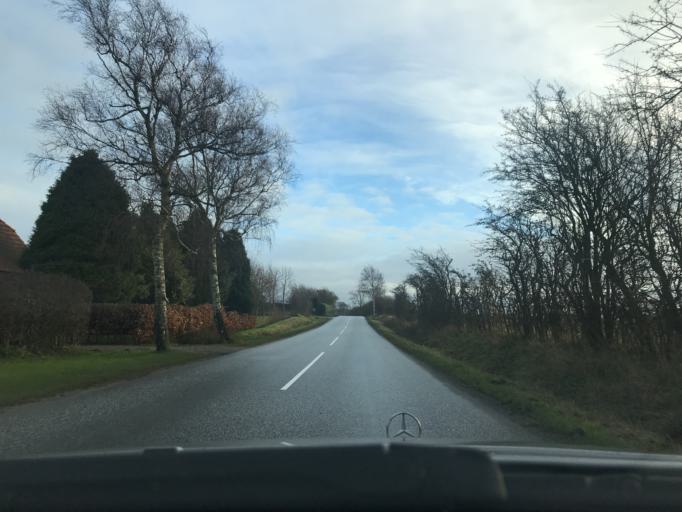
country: DK
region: South Denmark
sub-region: Sonderborg Kommune
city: Broager
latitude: 54.8851
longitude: 9.6917
